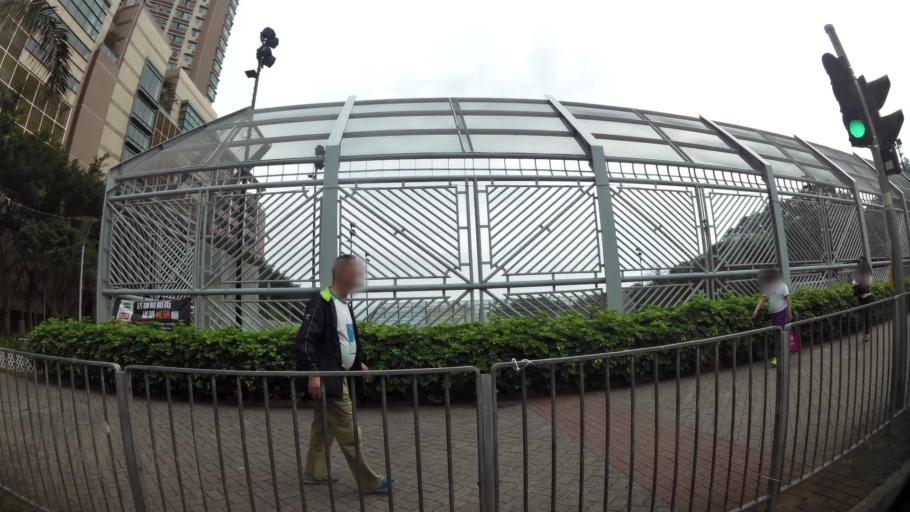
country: HK
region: Wanchai
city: Wan Chai
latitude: 22.2651
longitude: 114.2514
